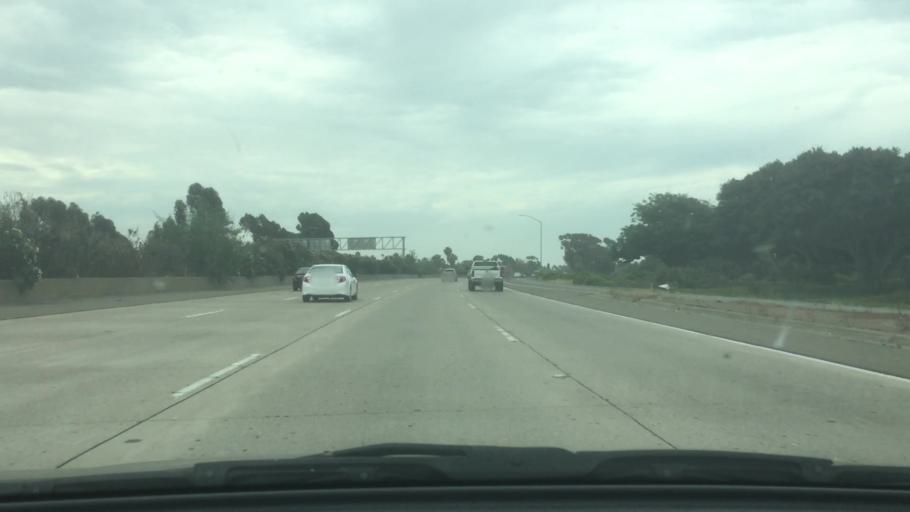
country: US
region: California
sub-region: San Diego County
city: La Jolla
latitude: 32.7896
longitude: -117.2072
